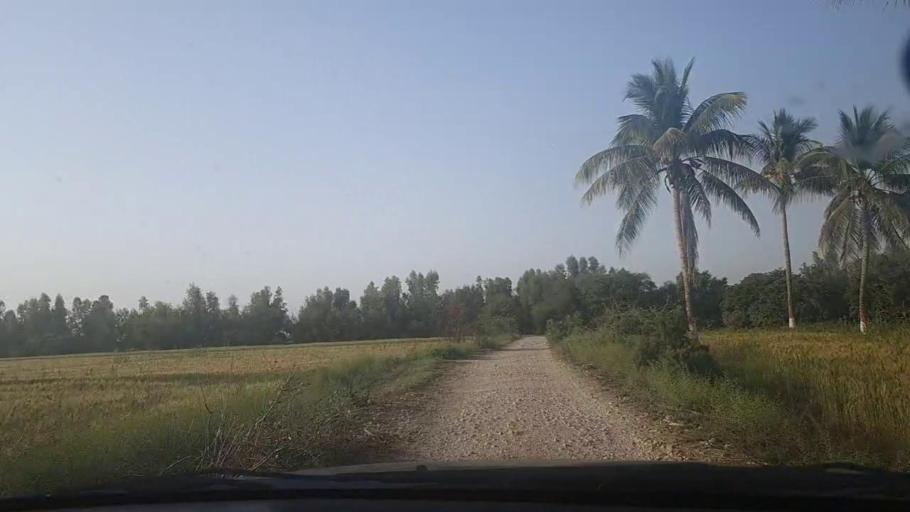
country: PK
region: Sindh
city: Keti Bandar
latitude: 24.2741
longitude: 67.5980
